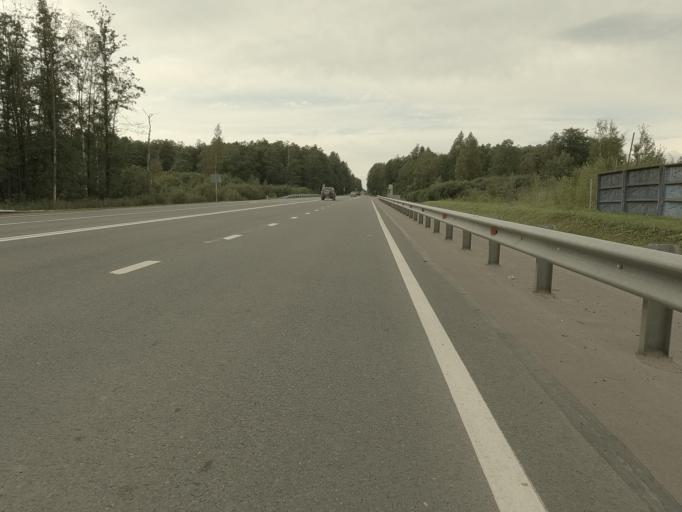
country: RU
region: Leningrad
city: Kirovsk
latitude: 59.8448
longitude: 31.0436
